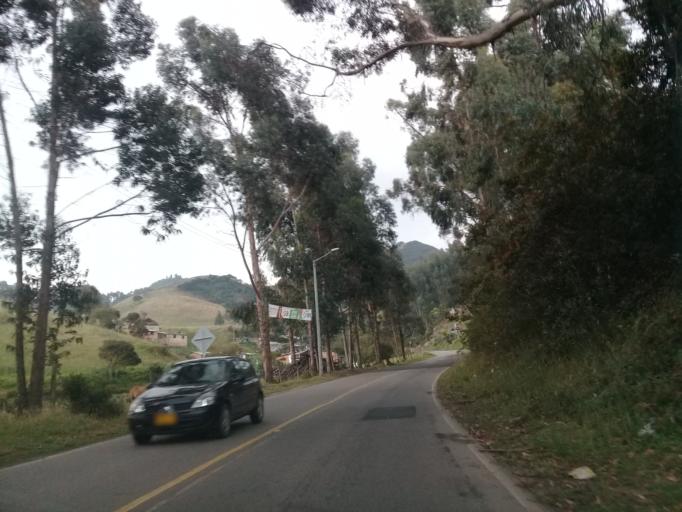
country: CO
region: Cundinamarca
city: Zipaquira
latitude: 5.0424
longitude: -74.0484
